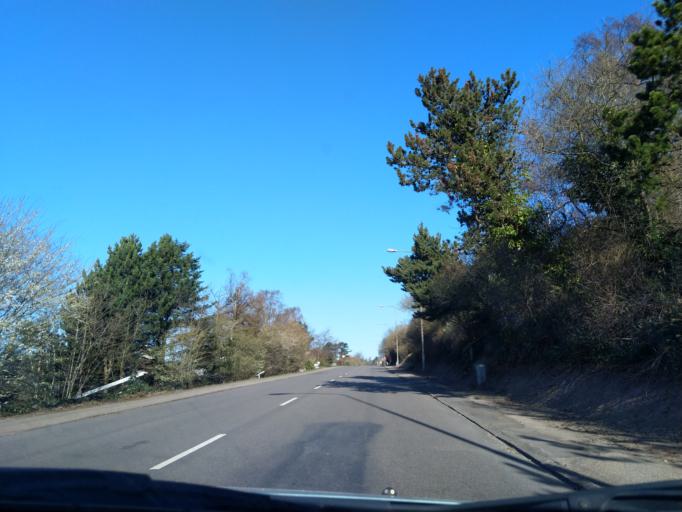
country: DK
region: Zealand
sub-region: Kalundborg Kommune
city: Kalundborg
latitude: 55.6945
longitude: 11.0469
